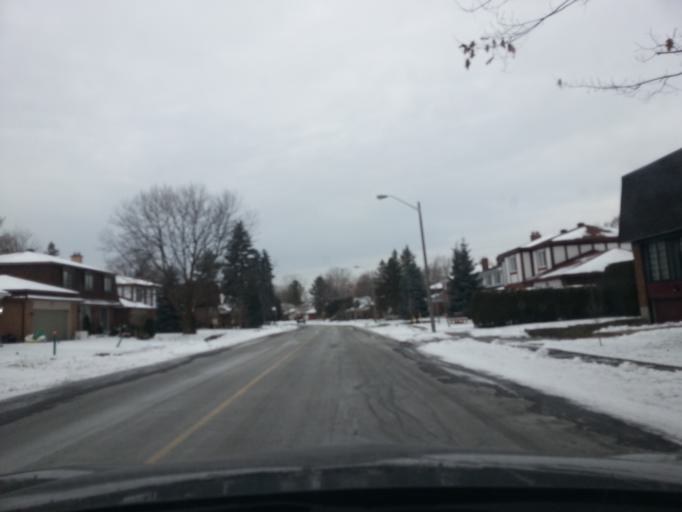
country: CA
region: Ontario
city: Ottawa
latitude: 45.3569
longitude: -75.6630
